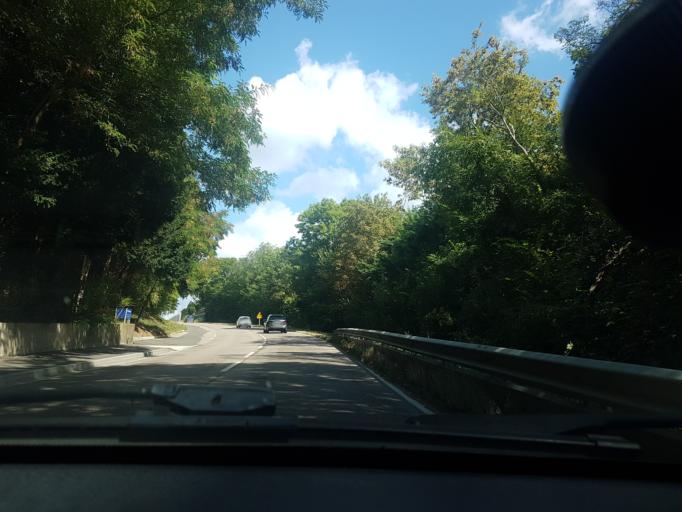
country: FR
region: Ile-de-France
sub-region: Departement des Yvelines
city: Saint-Nom-la-Breteche
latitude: 48.8457
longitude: 2.0168
